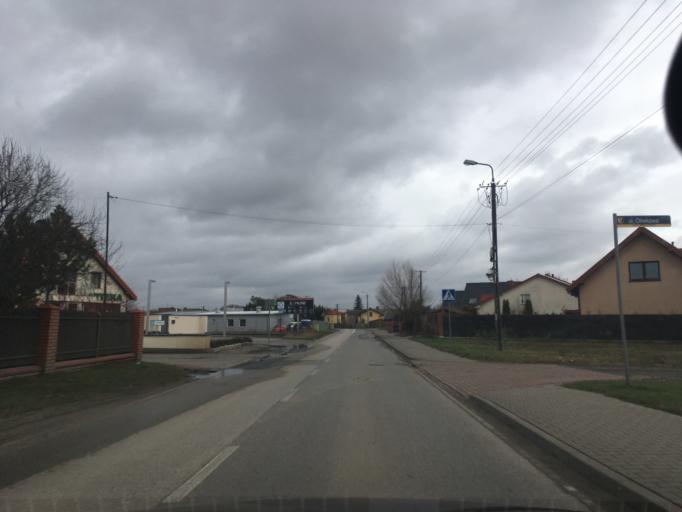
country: PL
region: Masovian Voivodeship
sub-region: Powiat pruszkowski
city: Rybie
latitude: 52.1245
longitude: 20.9533
